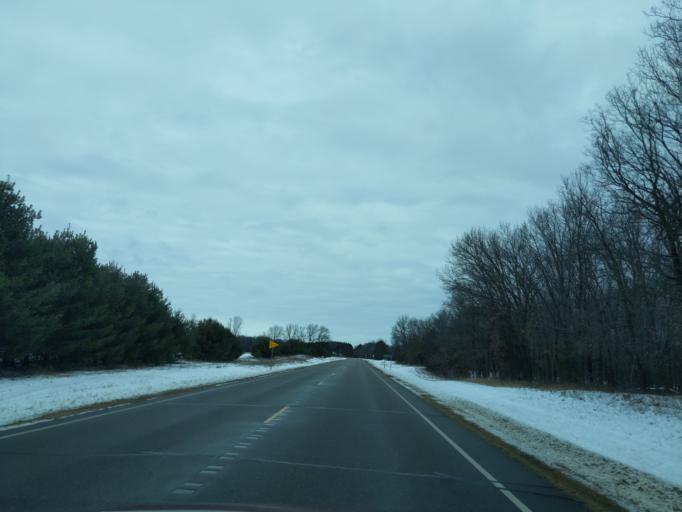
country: US
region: Wisconsin
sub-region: Marquette County
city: Montello
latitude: 43.9316
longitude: -89.3122
